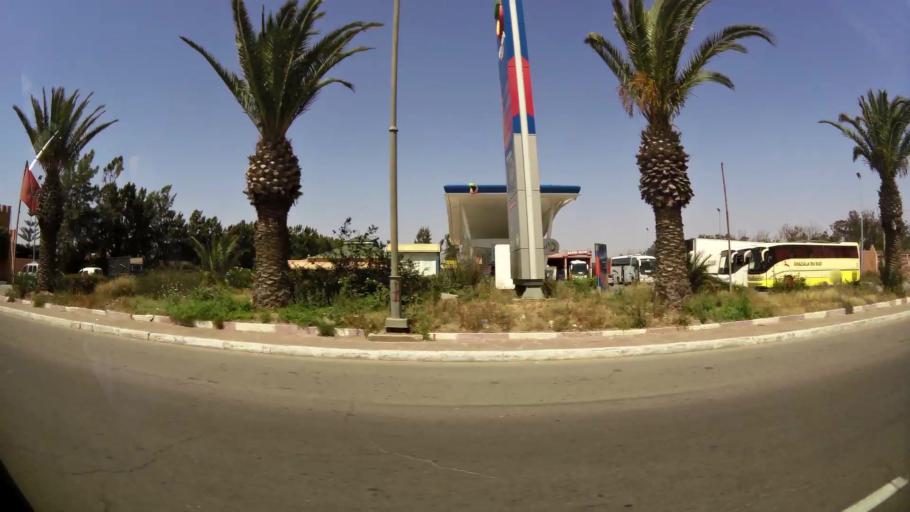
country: MA
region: Souss-Massa-Draa
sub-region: Inezgane-Ait Mellou
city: Inezgane
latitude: 30.3571
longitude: -9.5178
